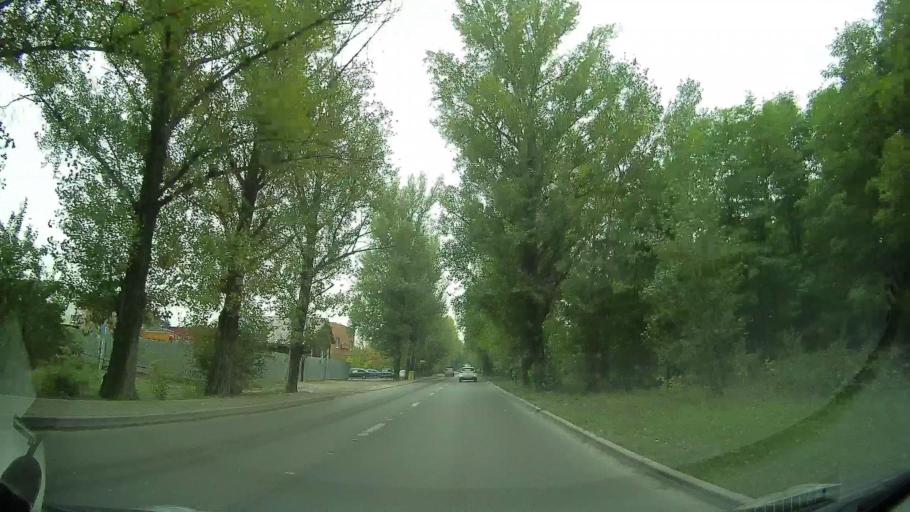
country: RU
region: Rostov
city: Severnyy
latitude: 47.2905
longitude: 39.6610
